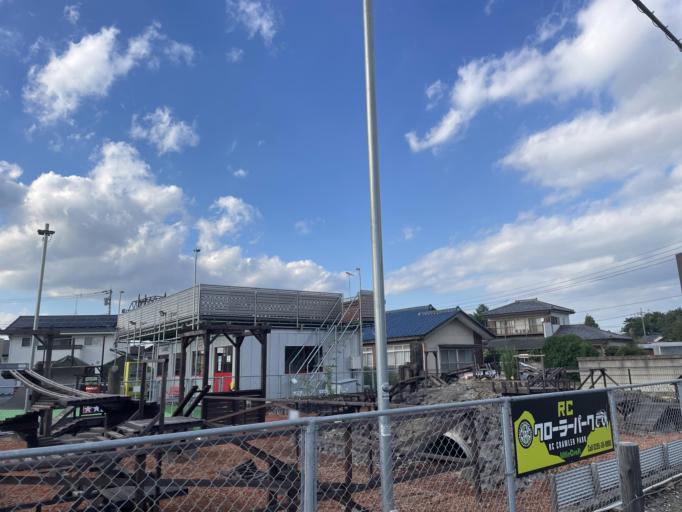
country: JP
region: Tochigi
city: Oyama
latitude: 36.2833
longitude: 139.7783
